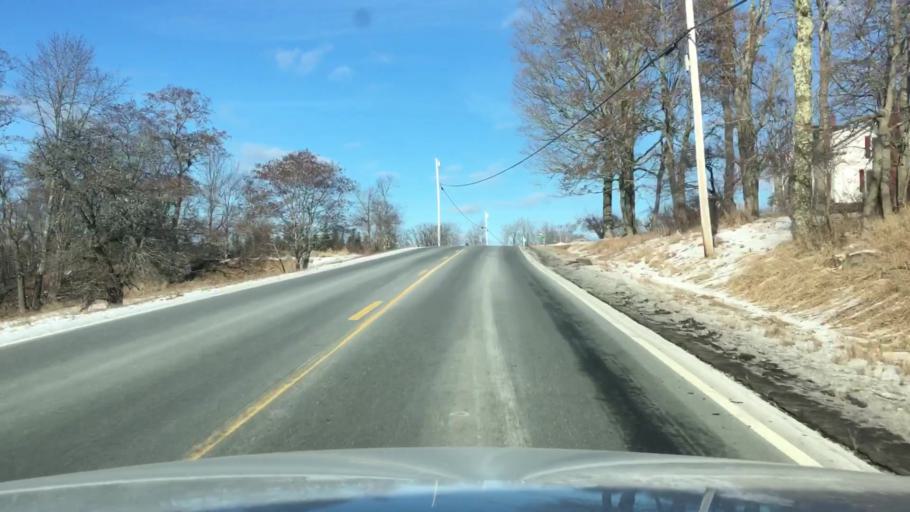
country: US
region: Maine
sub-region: Penobscot County
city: Holden
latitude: 44.7641
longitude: -68.5946
